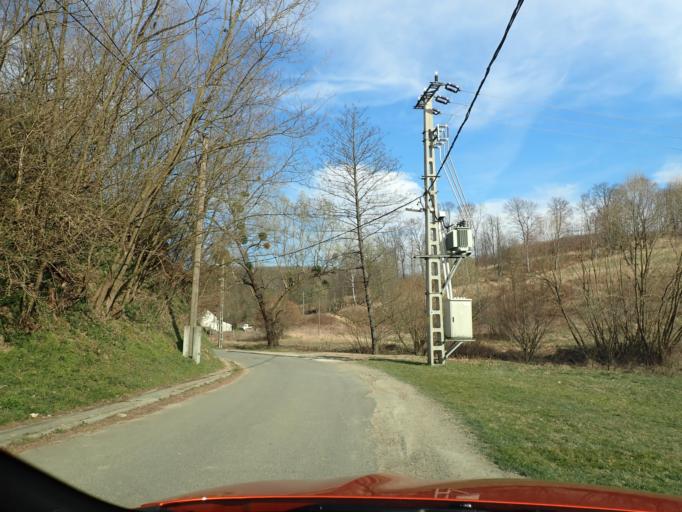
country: HU
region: Baranya
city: Komlo
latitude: 46.1625
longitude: 18.2560
